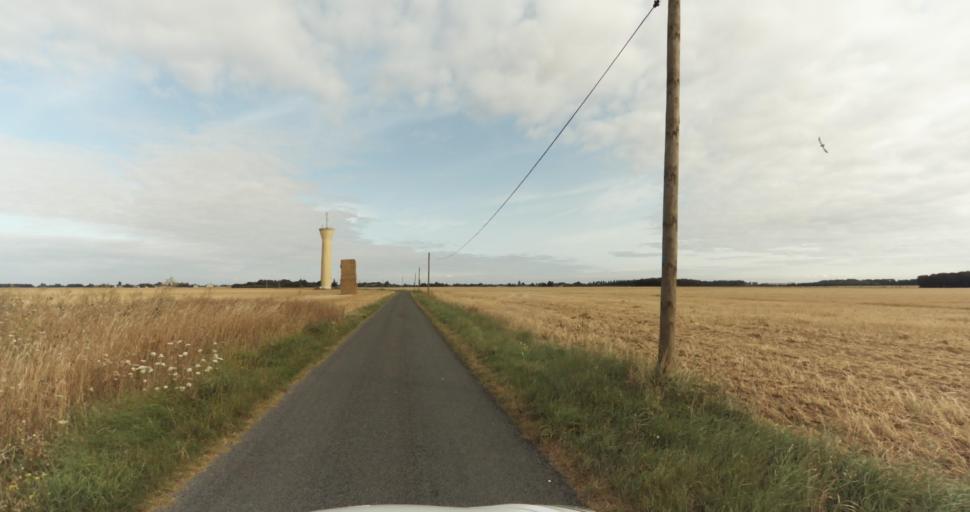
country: FR
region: Haute-Normandie
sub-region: Departement de l'Eure
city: La Madeleine-de-Nonancourt
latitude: 48.8701
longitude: 1.2420
